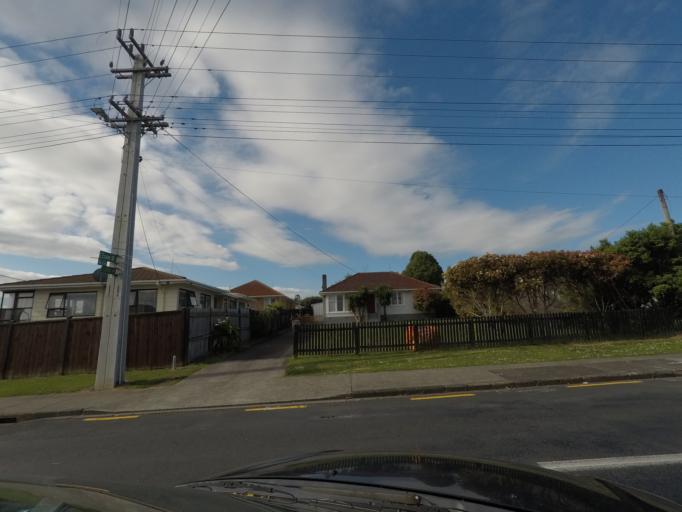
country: NZ
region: Auckland
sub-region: Auckland
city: Rosebank
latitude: -36.8697
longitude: 174.6451
